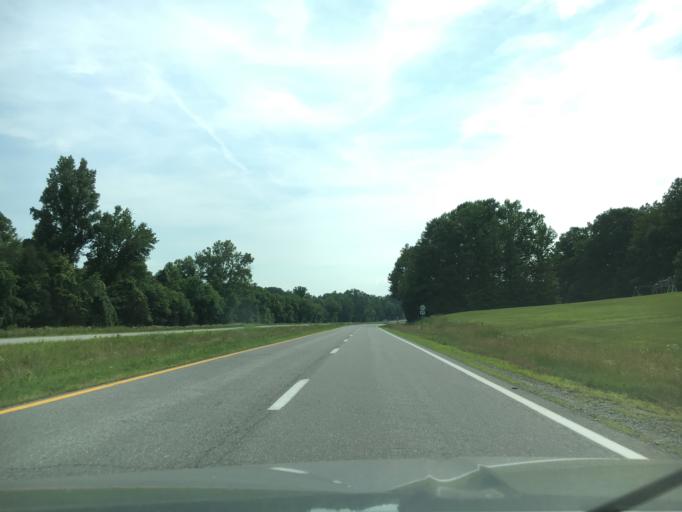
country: US
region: Virginia
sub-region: Mecklenburg County
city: Chase City
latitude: 36.8422
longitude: -78.6277
